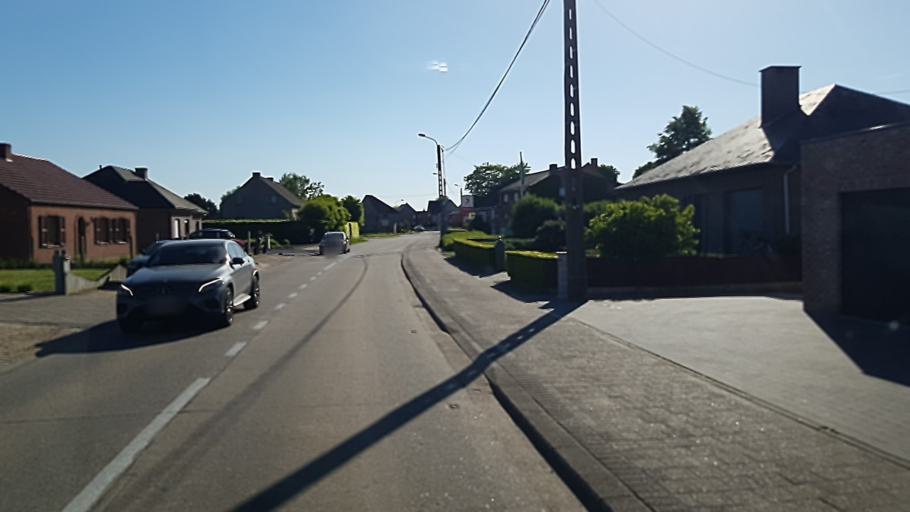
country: BE
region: Flanders
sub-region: Provincie Antwerpen
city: Berlaar
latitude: 51.0834
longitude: 4.6781
